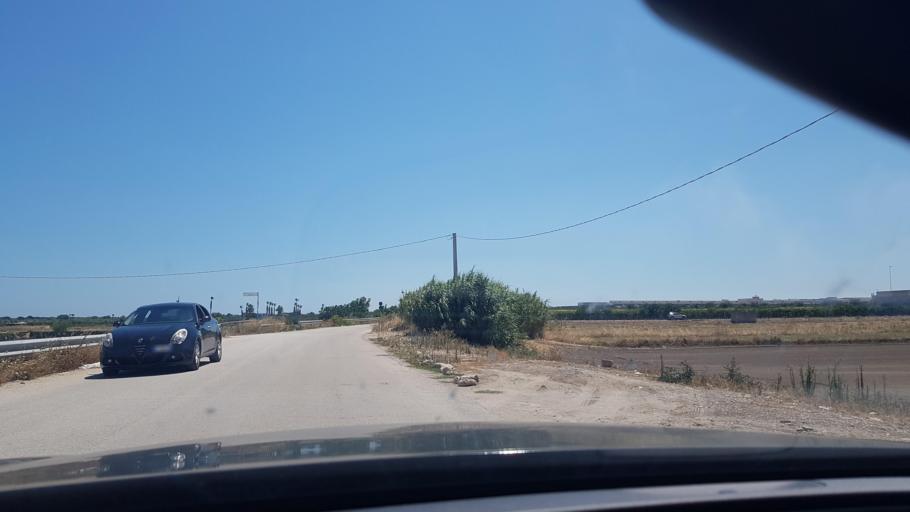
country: IT
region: Apulia
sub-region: Provincia di Barletta - Andria - Trani
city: Barletta
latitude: 41.3104
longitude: 16.3221
